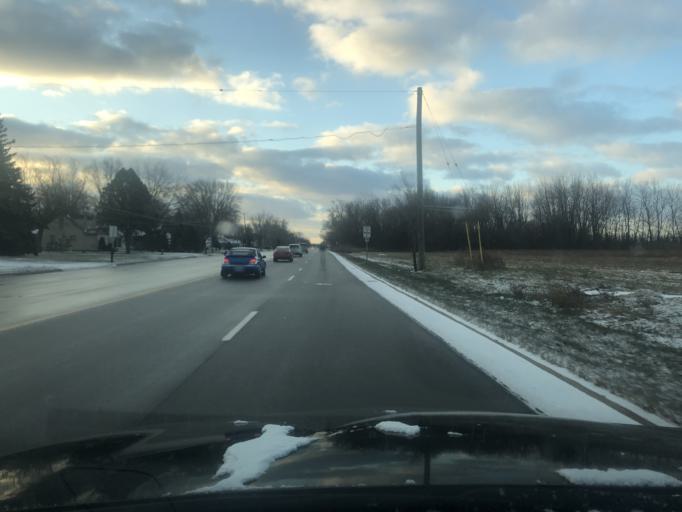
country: US
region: Michigan
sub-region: Wayne County
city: Wayne
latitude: 42.2599
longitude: -83.3481
